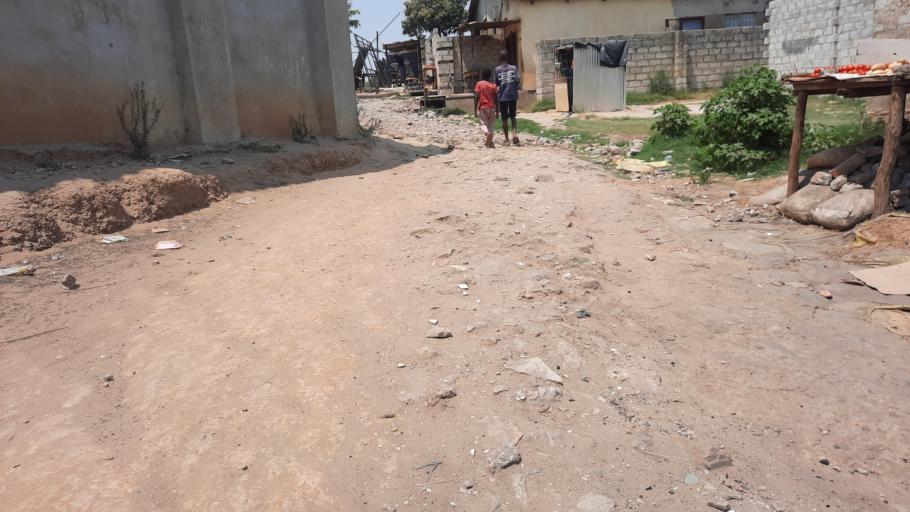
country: ZM
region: Lusaka
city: Lusaka
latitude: -15.4046
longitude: 28.3811
